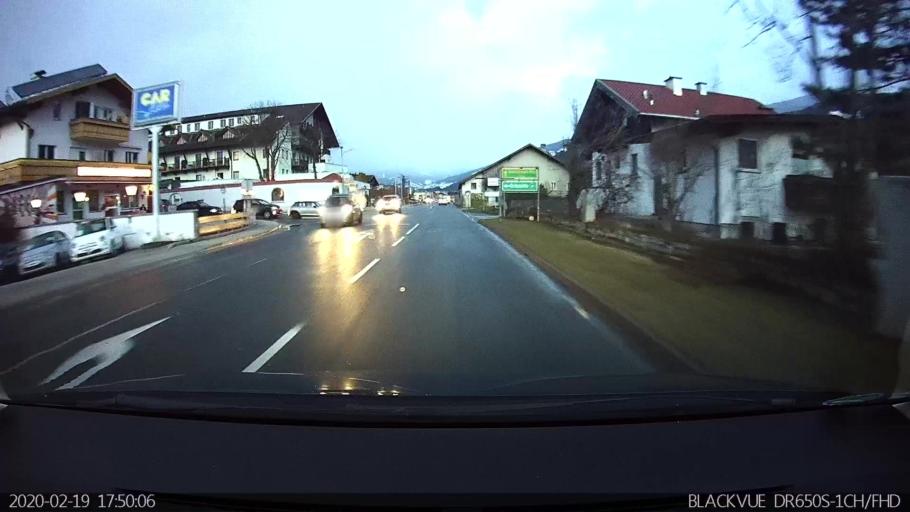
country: AT
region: Tyrol
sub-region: Politischer Bezirk Innsbruck Land
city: Hall in Tirol
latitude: 47.2802
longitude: 11.5283
